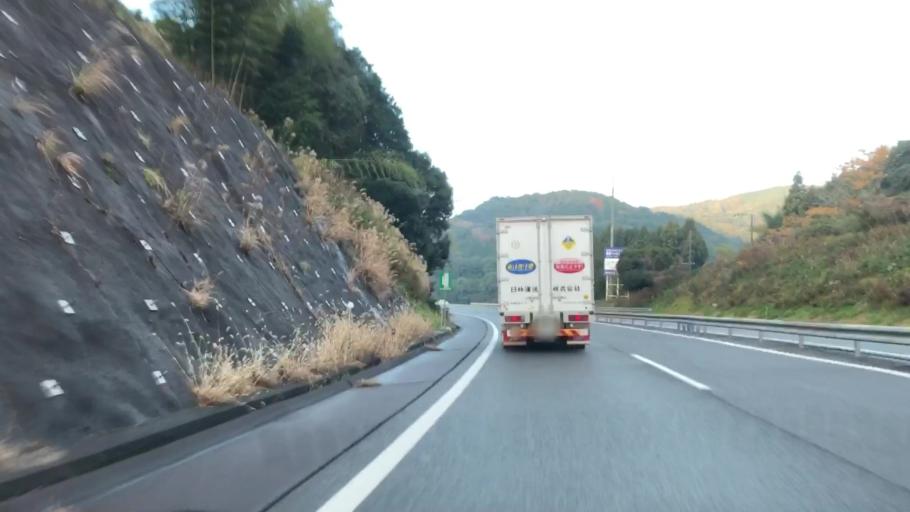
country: JP
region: Nagasaki
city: Sasebo
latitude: 33.1629
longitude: 129.8251
